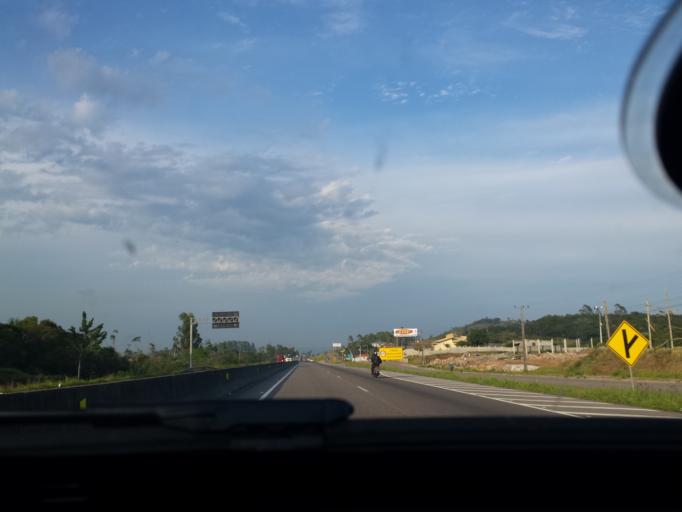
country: BR
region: Santa Catarina
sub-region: Tubarao
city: Tubarao
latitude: -28.4257
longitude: -48.9050
